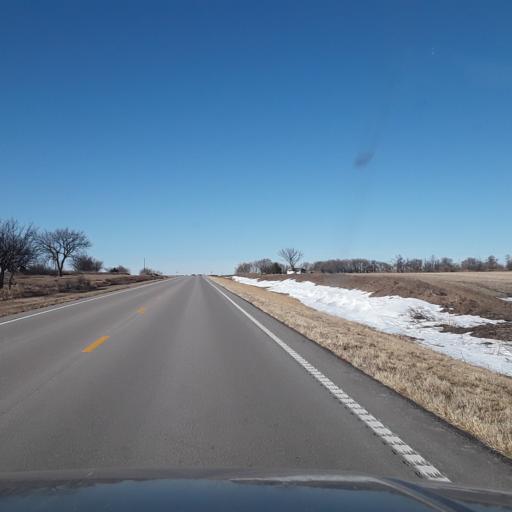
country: US
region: Nebraska
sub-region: Dawson County
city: Cozad
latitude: 40.6739
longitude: -100.1098
